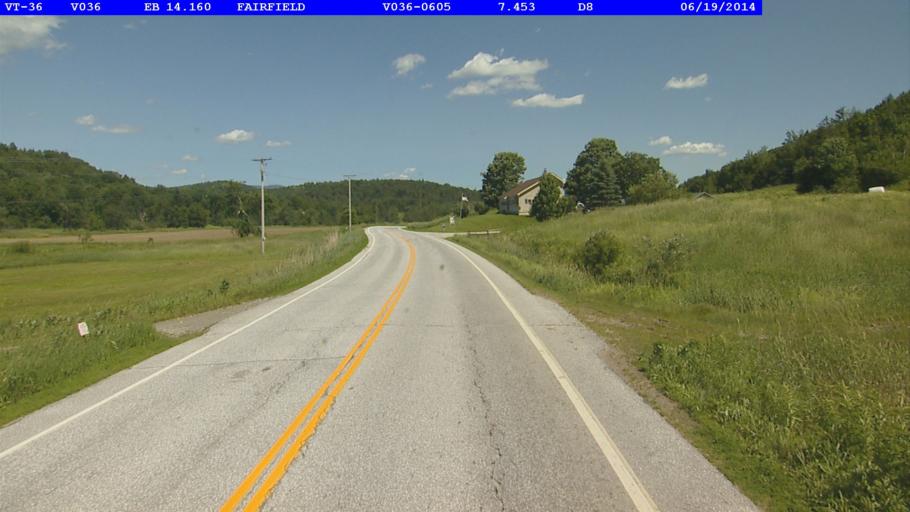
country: US
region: Vermont
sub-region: Franklin County
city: Enosburg Falls
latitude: 44.7995
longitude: -72.8915
